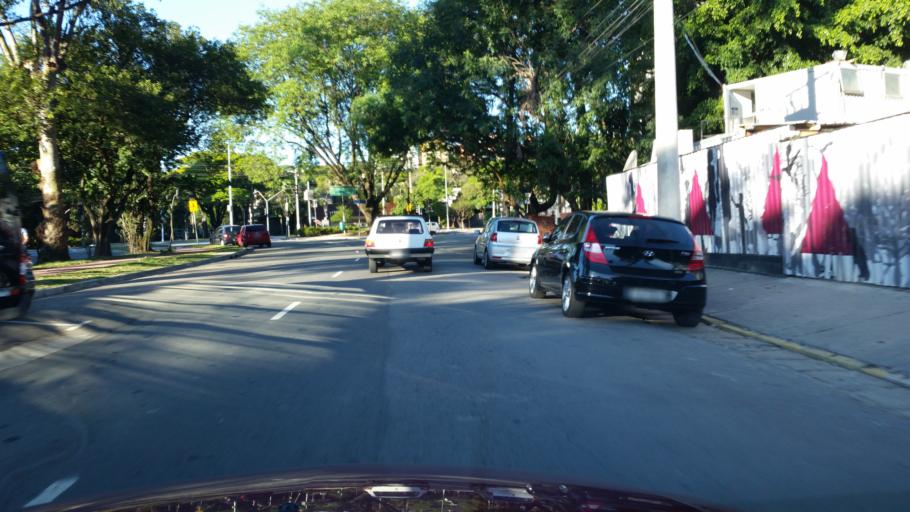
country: BR
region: Sao Paulo
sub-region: Sao Paulo
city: Sao Paulo
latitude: -23.5592
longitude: -46.6994
